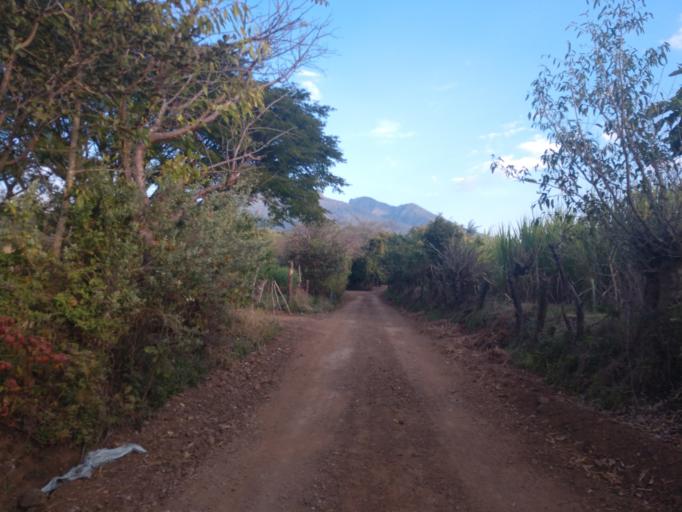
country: MX
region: Nayarit
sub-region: Tepic
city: La Corregidora
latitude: 21.4560
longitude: -104.7914
